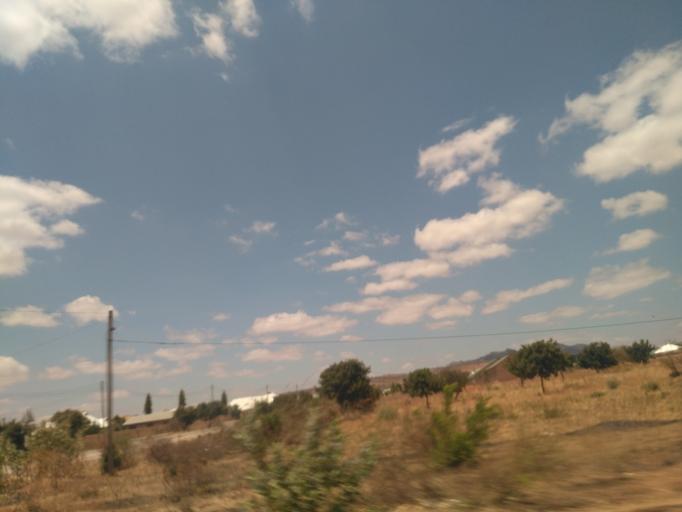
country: TZ
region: Dodoma
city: Kisasa
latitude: -6.1727
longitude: 35.7993
